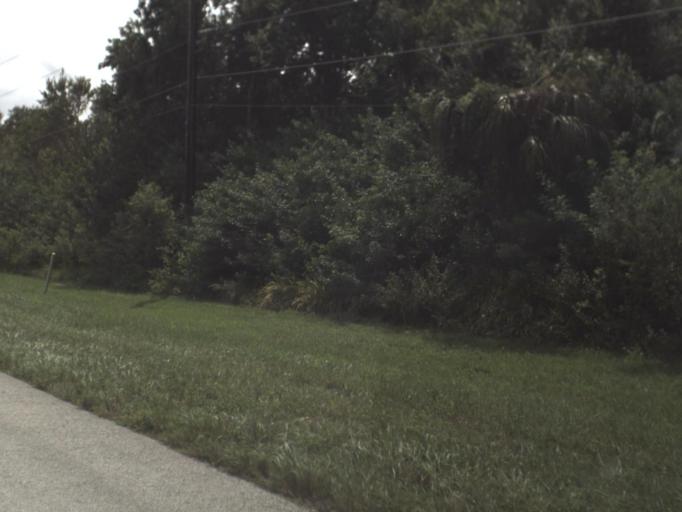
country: US
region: Florida
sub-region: Hillsborough County
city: Ruskin
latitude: 27.5965
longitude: -82.4256
